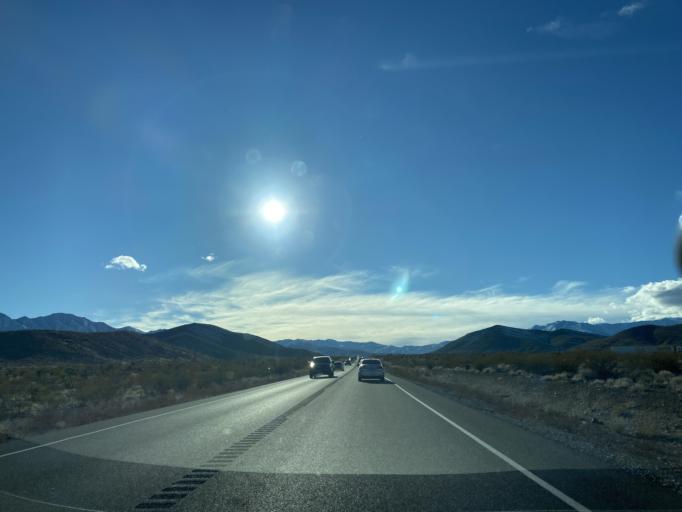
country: US
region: Nevada
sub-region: Clark County
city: Summerlin South
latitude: 36.2951
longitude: -115.4214
